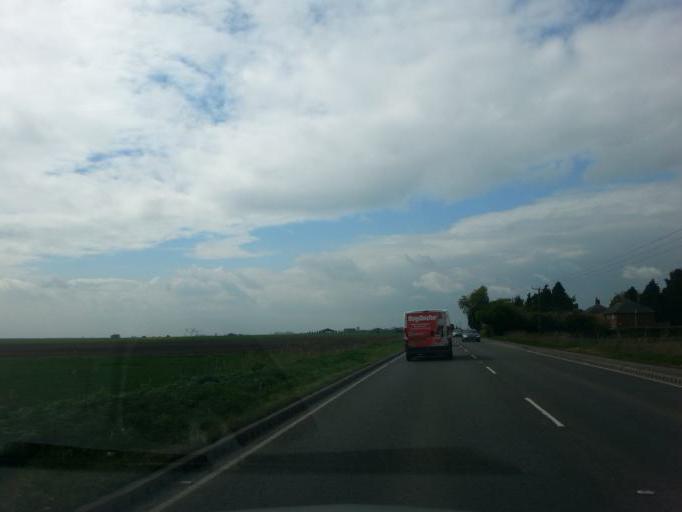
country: GB
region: England
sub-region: Cambridgeshire
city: March
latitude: 52.6082
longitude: 0.0515
